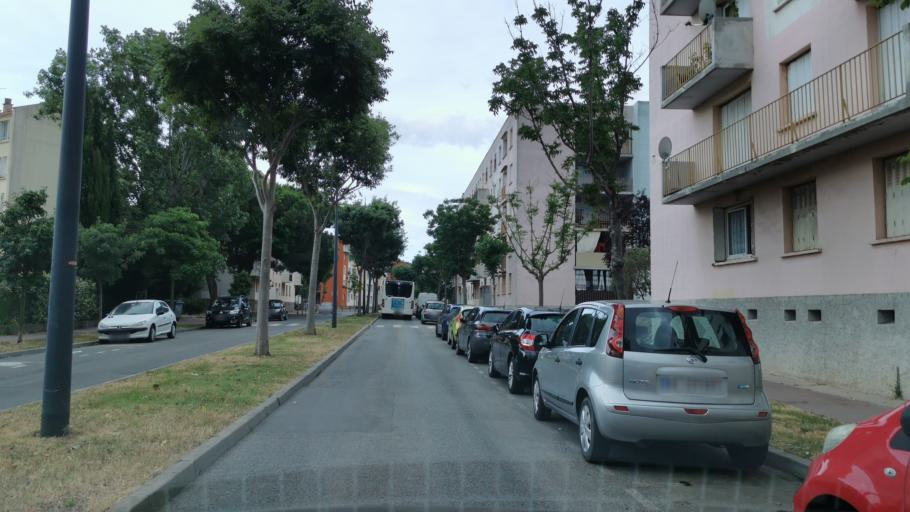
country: FR
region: Languedoc-Roussillon
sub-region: Departement de l'Aude
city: Narbonne
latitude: 43.1949
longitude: 3.0148
